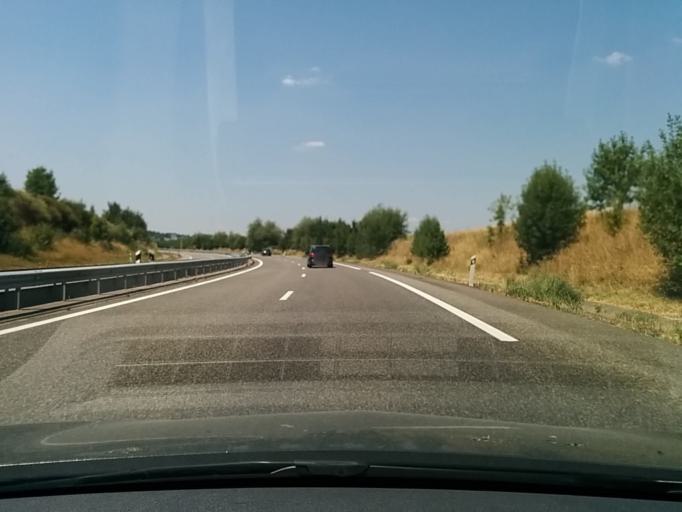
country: FR
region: Midi-Pyrenees
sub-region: Departement du Gers
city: Pujaudran
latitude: 43.6049
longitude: 1.0784
